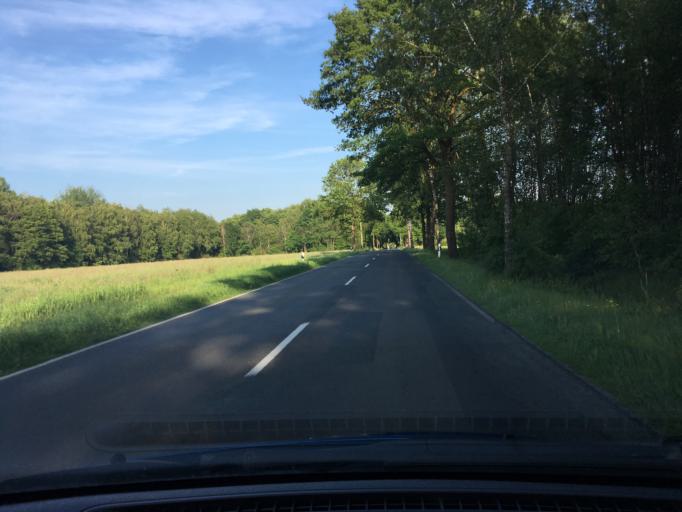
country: DE
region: Lower Saxony
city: Otter
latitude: 53.2565
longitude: 9.7475
